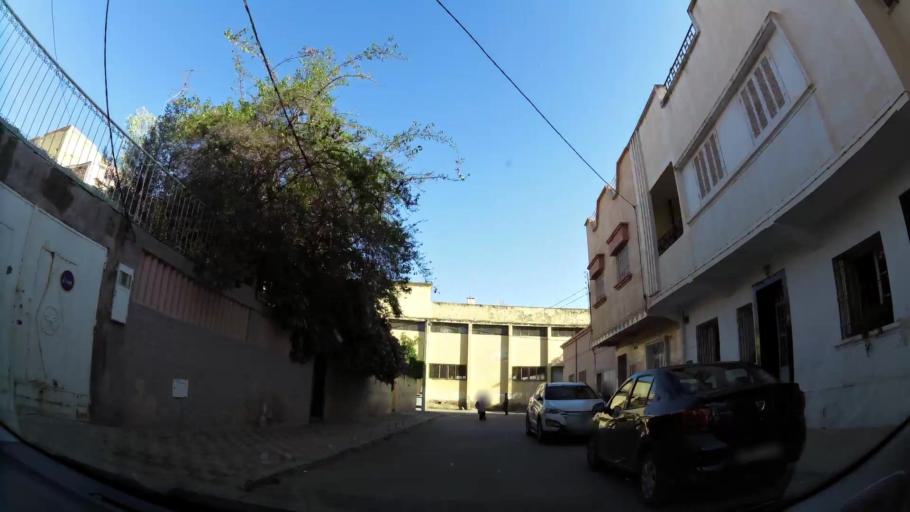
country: MA
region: Oriental
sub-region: Oujda-Angad
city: Oujda
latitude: 34.6914
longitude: -1.9170
